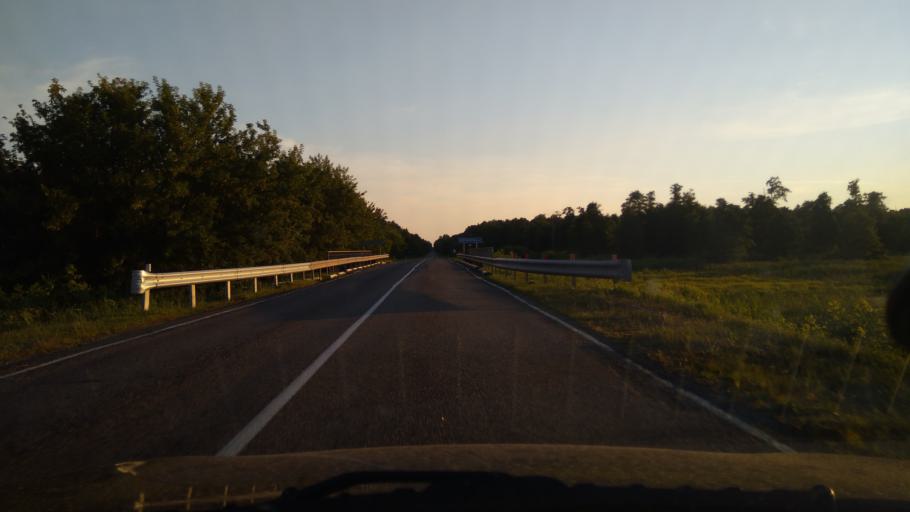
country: BY
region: Brest
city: Nyakhachava
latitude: 52.6162
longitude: 25.1498
